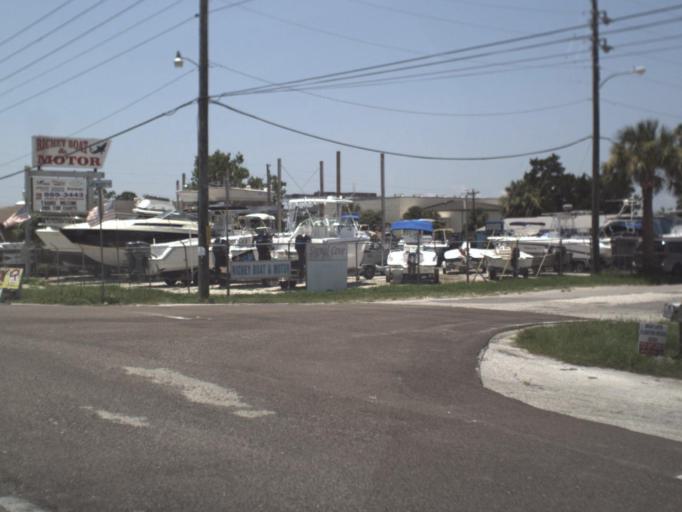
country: US
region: Florida
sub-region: Pasco County
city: Hudson
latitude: 28.3498
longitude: -82.6993
